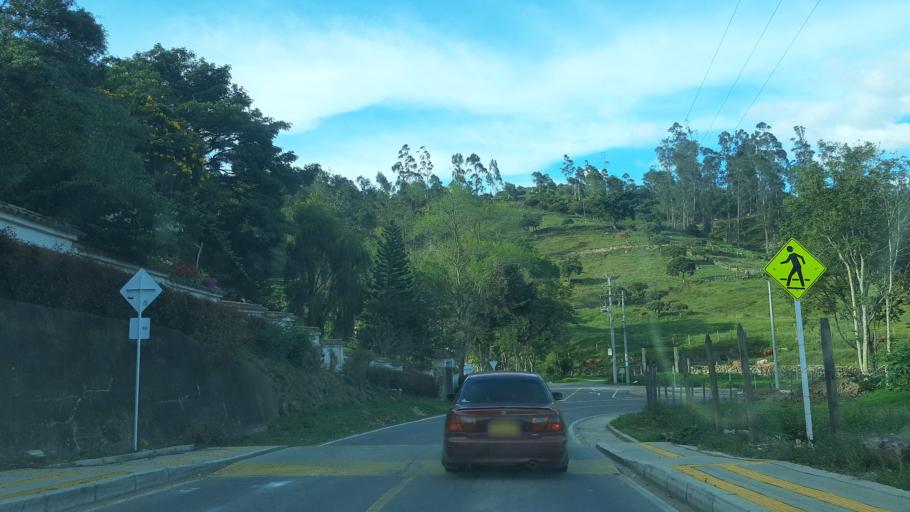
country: CO
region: Cundinamarca
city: Macheta
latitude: 5.0798
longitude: -73.6046
